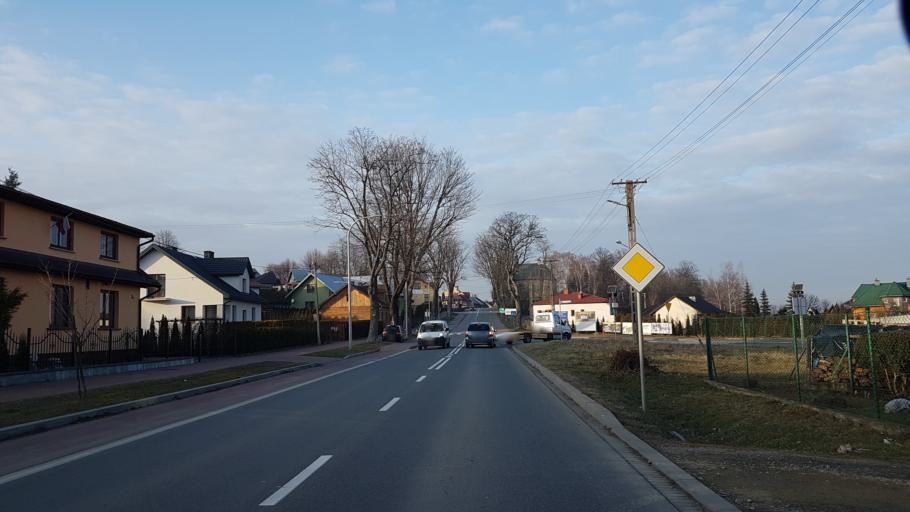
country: PL
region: Lesser Poland Voivodeship
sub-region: Powiat nowosadecki
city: Stary Sacz
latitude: 49.5550
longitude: 20.6388
